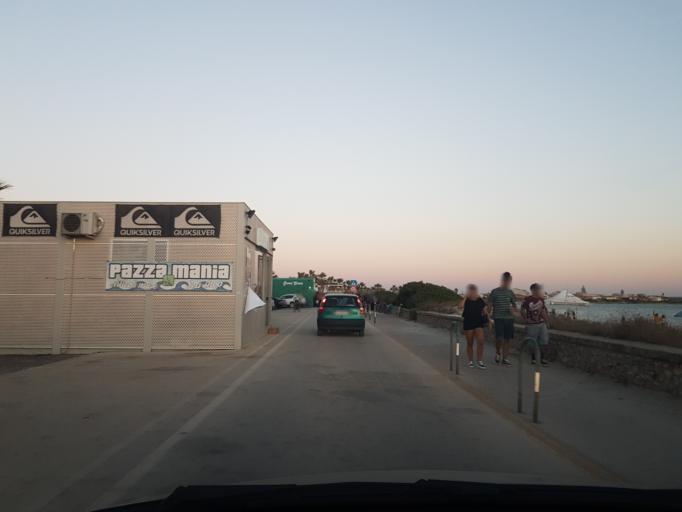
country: IT
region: Sardinia
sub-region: Provincia di Oristano
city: Riola Sardo
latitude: 40.0316
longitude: 8.4037
